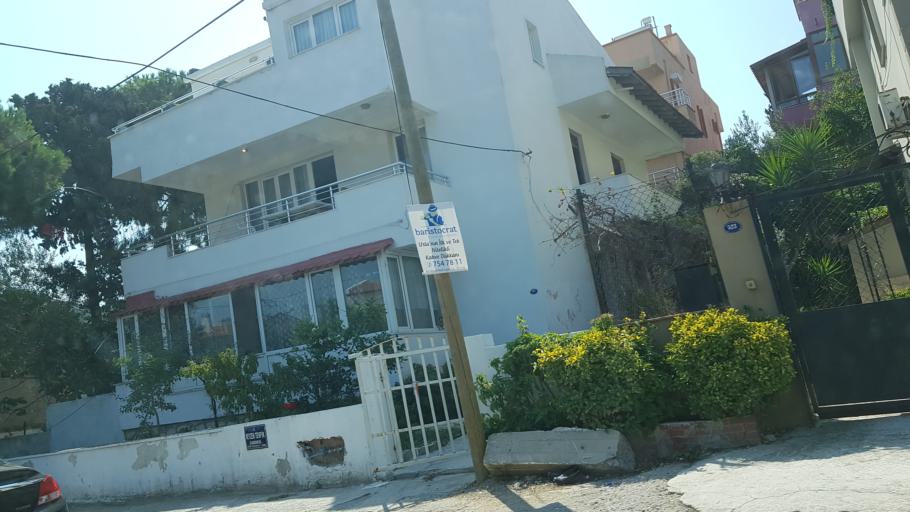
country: TR
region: Izmir
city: Urla
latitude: 38.3639
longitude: 26.7675
